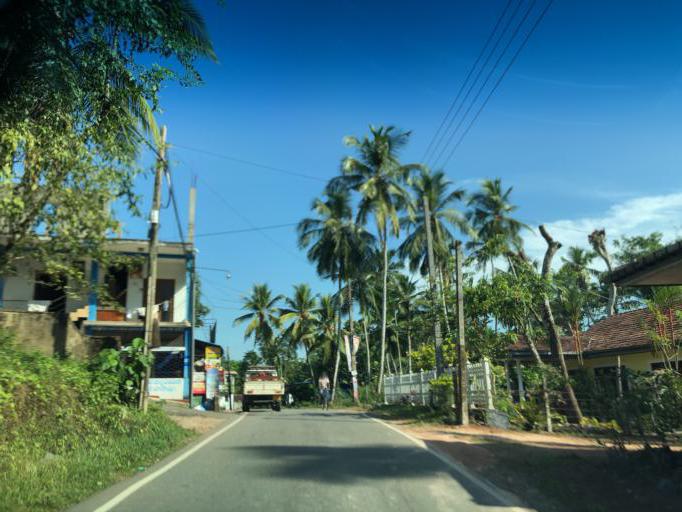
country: LK
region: Western
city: Homagama
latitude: 6.7879
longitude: 79.9789
